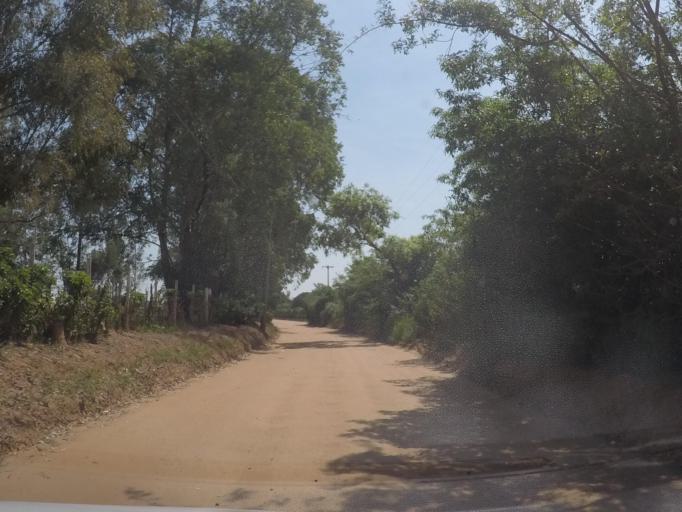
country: BR
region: Sao Paulo
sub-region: Sumare
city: Sumare
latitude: -22.8826
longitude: -47.2931
